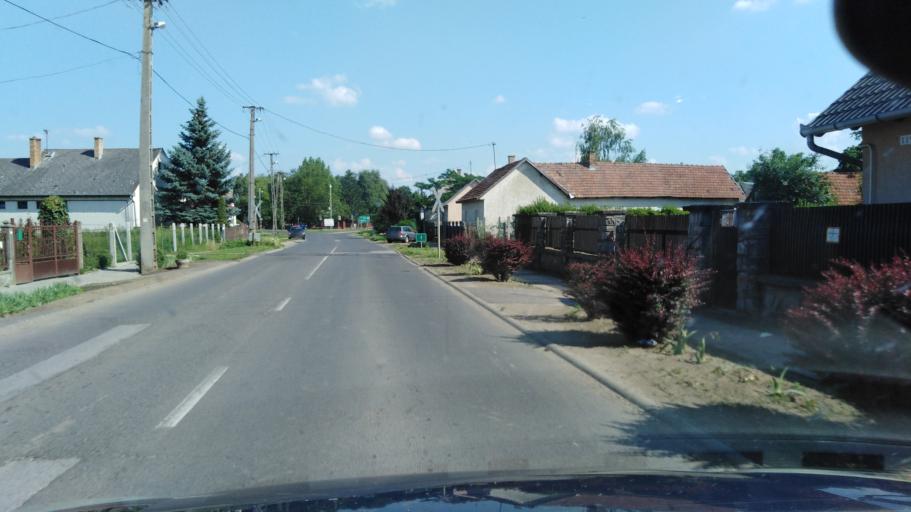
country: HU
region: Szabolcs-Szatmar-Bereg
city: Nyirbator
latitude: 47.8276
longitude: 22.1424
